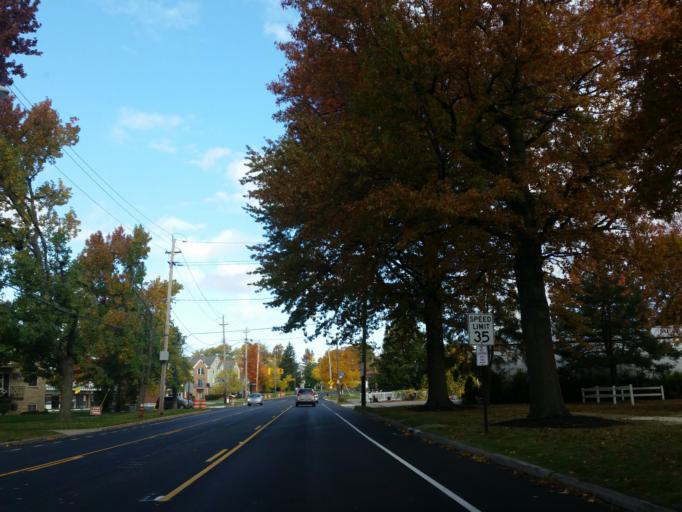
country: US
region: Ohio
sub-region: Cuyahoga County
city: Brooklyn Heights
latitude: 41.4228
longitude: -81.6963
